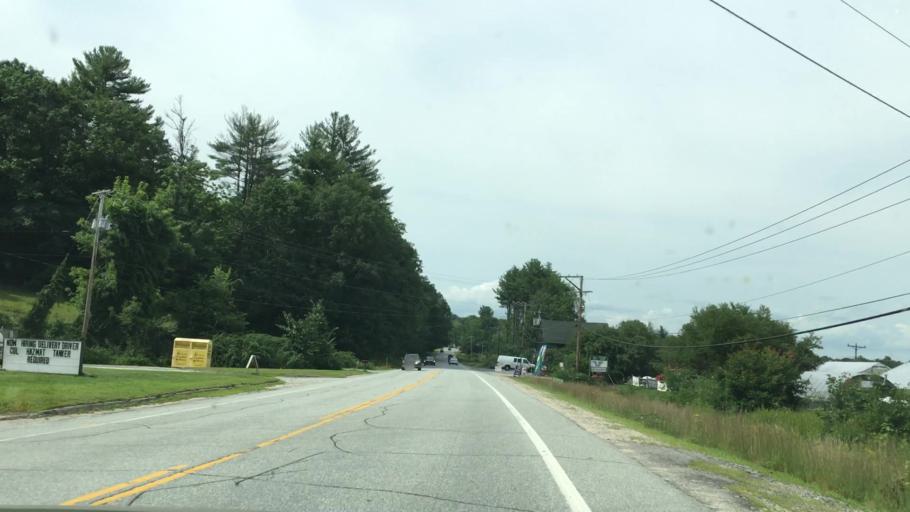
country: US
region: New Hampshire
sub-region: Hillsborough County
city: Antrim
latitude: 43.0193
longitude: -71.9343
